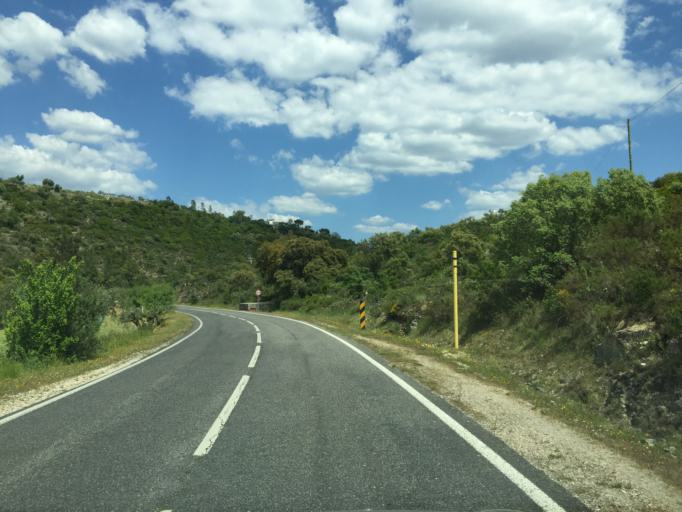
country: PT
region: Santarem
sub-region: Ourem
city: Fatima
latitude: 39.6412
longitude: -8.6367
